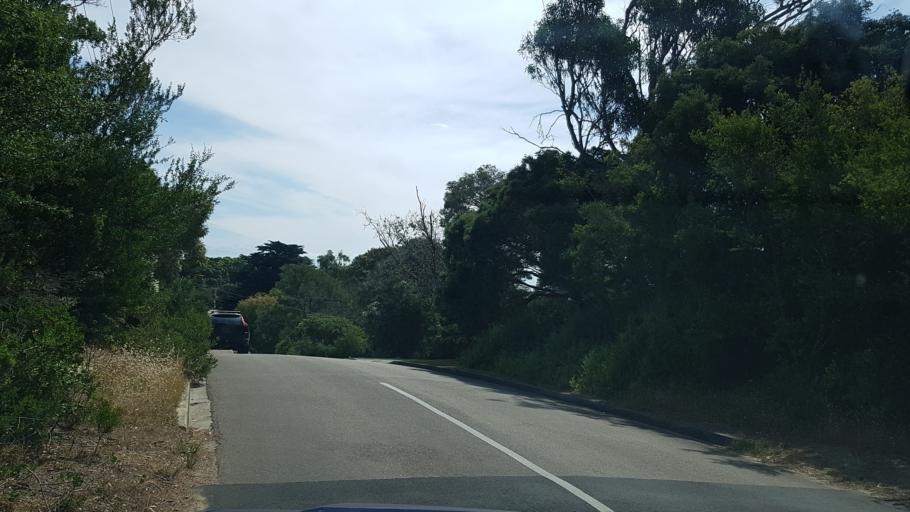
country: AU
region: Victoria
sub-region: Mornington Peninsula
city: Sorrento
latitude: -38.3237
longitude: 144.7176
